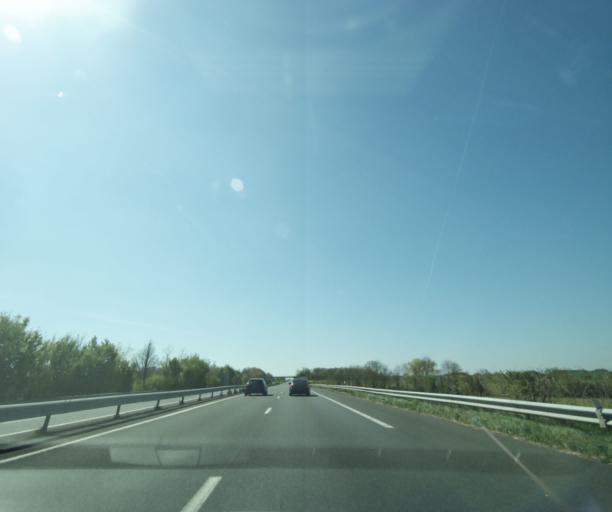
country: FR
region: Centre
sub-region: Departement de l'Indre
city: Vatan
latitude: 47.0420
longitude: 1.7954
